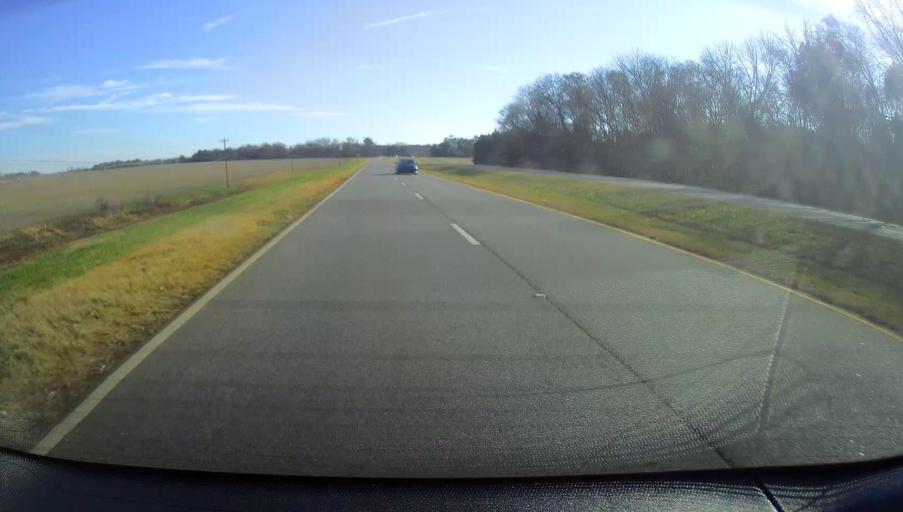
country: US
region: Alabama
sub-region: Morgan County
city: Decatur
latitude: 34.6862
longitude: -86.9521
